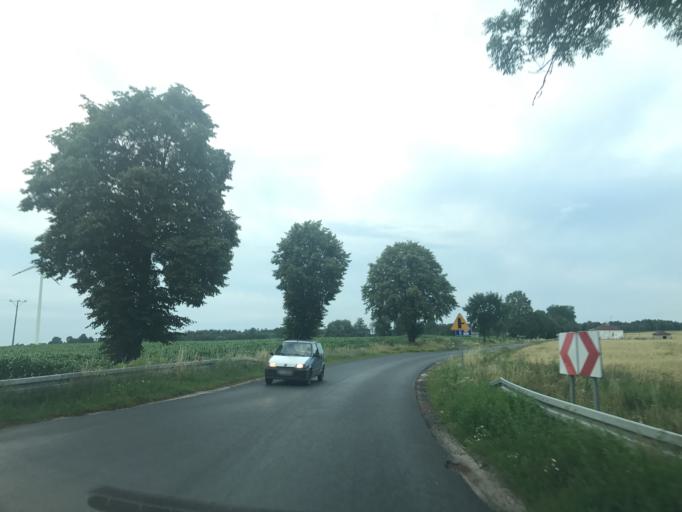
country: PL
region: Kujawsko-Pomorskie
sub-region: Powiat lipnowski
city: Lipno
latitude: 52.8099
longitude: 19.1846
